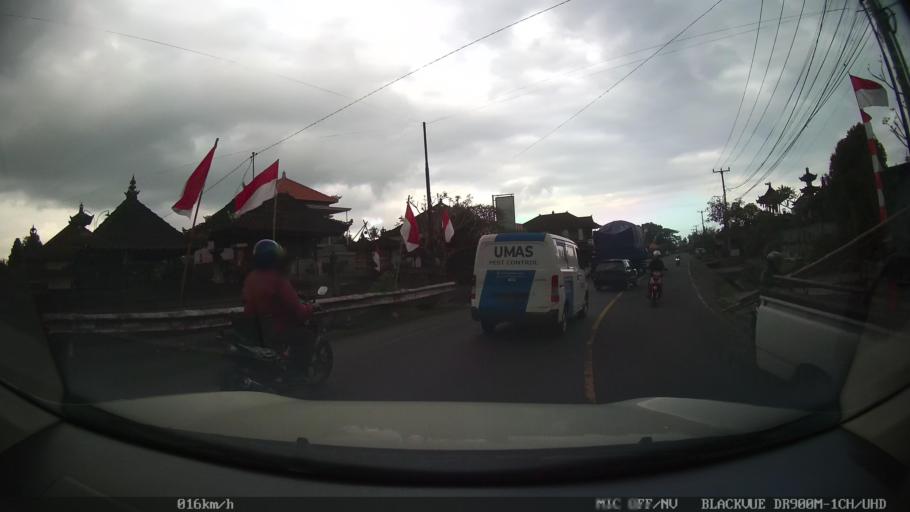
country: ID
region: Bali
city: Banjar Bantasbaleagung
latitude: -8.5049
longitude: 115.0717
